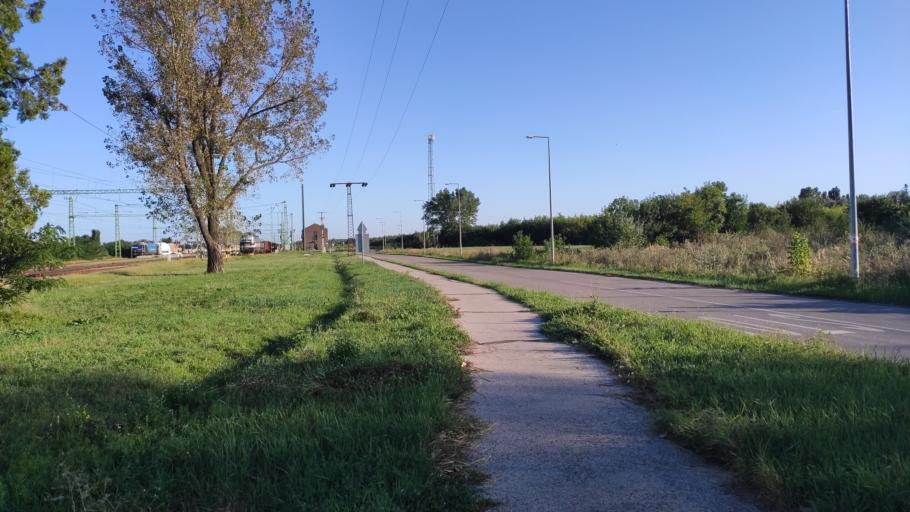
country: HU
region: Bekes
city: Mezobereny
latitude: 46.7589
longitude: 21.0370
